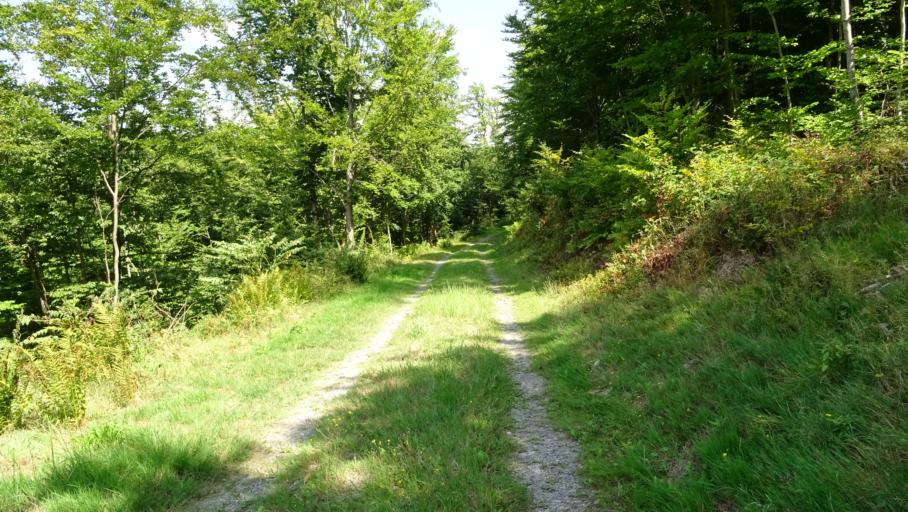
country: DE
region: Baden-Wuerttemberg
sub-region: Karlsruhe Region
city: Fahrenbach
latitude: 49.4176
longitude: 9.1115
